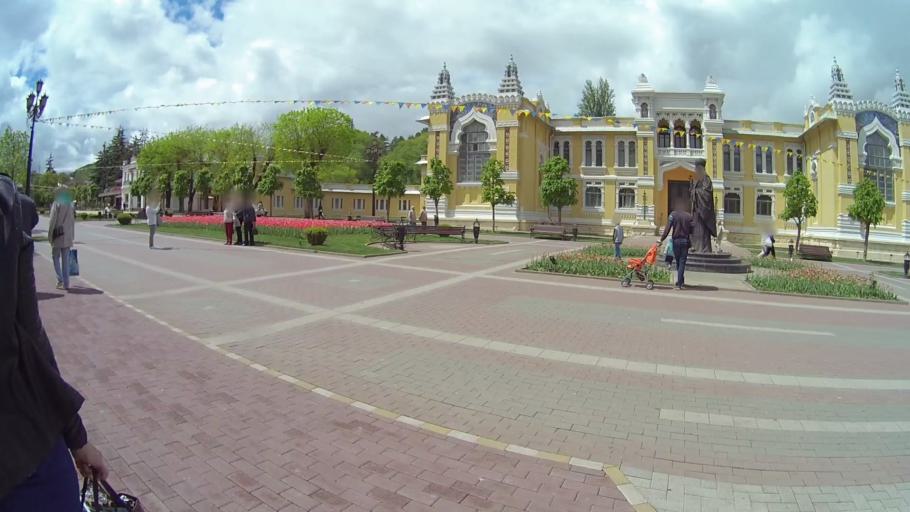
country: RU
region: Stavropol'skiy
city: Kislovodsk
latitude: 43.9023
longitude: 42.7170
